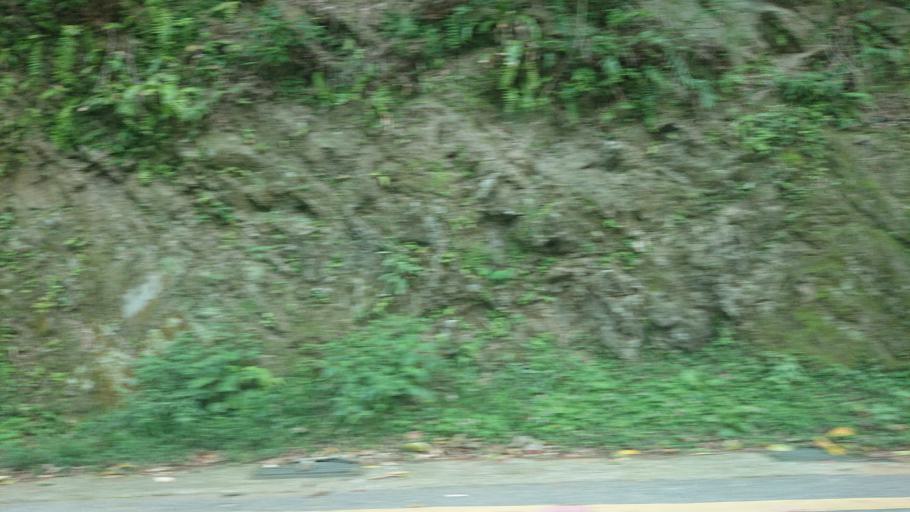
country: TW
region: Taiwan
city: Daxi
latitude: 24.8777
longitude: 121.3808
